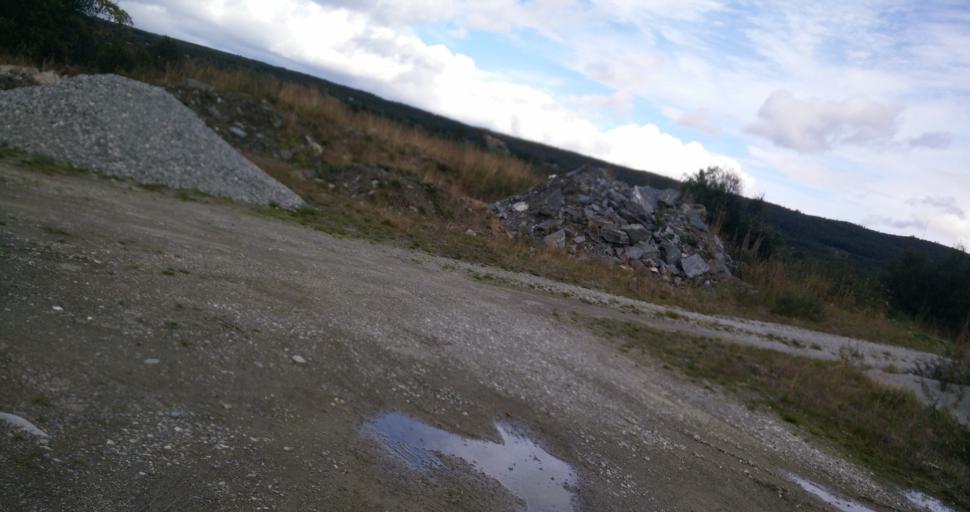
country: NO
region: Sor-Trondelag
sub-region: Tydal
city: Aas
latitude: 62.6337
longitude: 12.4188
